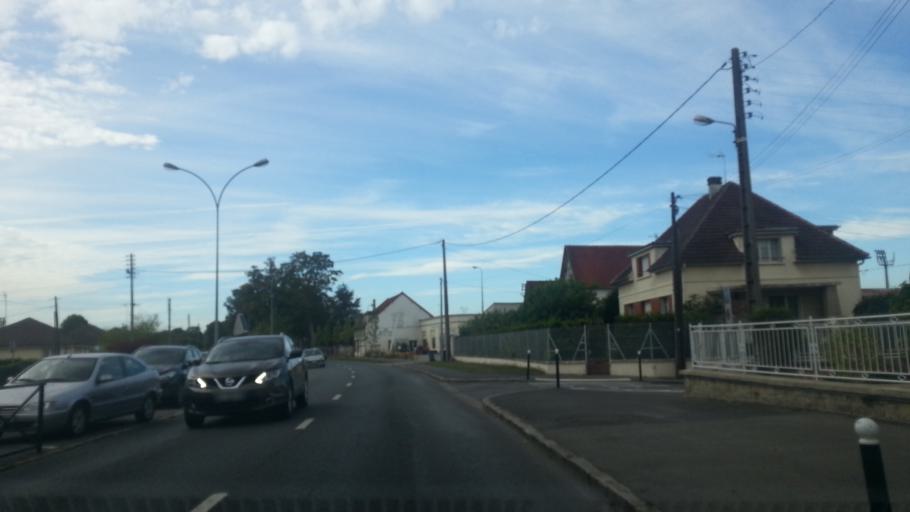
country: FR
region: Picardie
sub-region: Departement de l'Oise
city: Senlis
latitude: 49.2074
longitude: 2.5759
